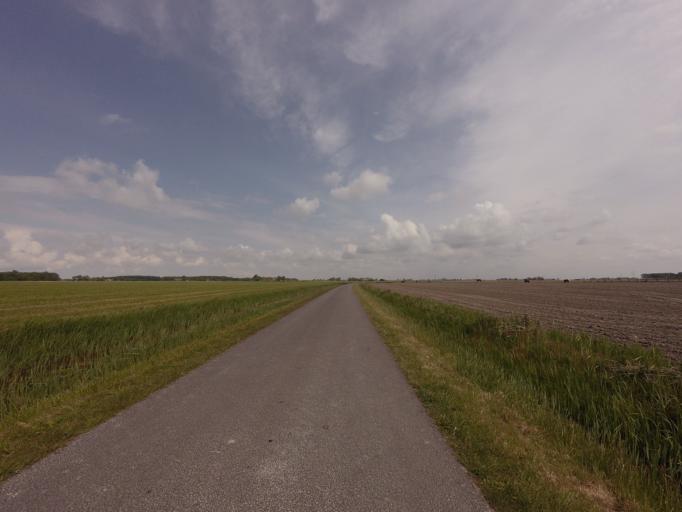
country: NL
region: Friesland
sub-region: Sudwest Fryslan
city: Bolsward
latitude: 53.1013
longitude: 5.4822
